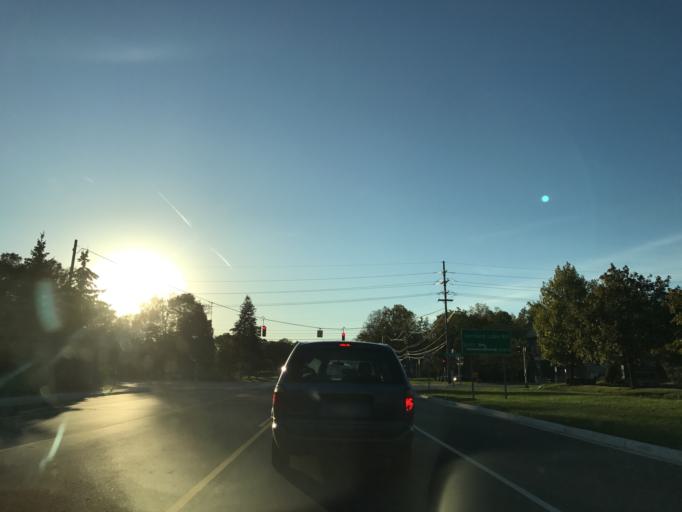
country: US
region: Michigan
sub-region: Oakland County
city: Farmington Hills
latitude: 42.4848
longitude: -83.3569
